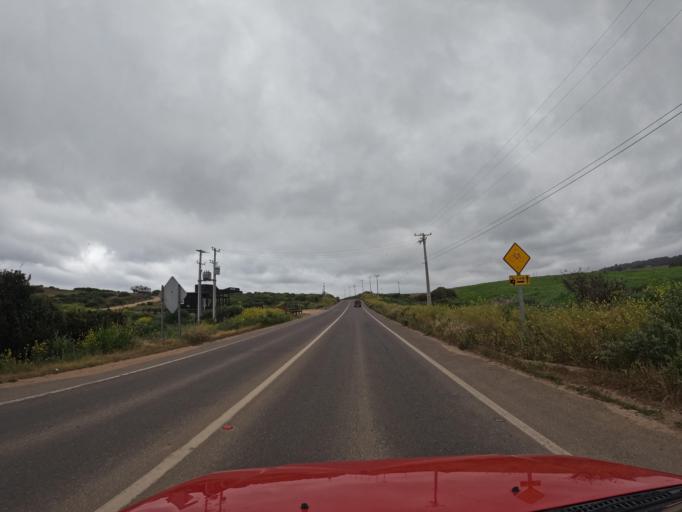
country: CL
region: O'Higgins
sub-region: Provincia de Colchagua
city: Santa Cruz
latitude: -34.4459
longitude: -72.0319
